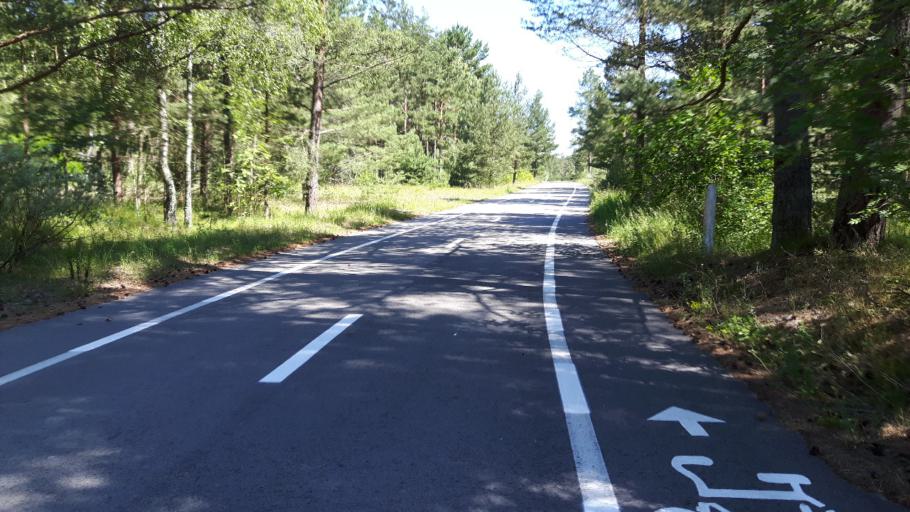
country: LT
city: Nida
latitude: 55.3224
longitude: 21.0244
